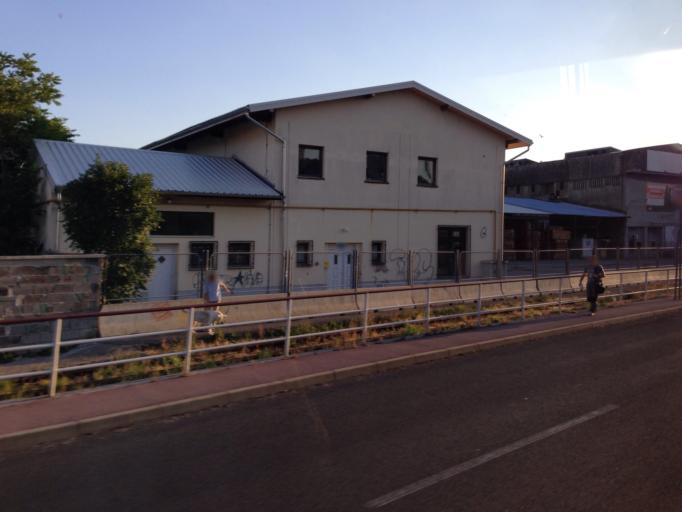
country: HR
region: Primorsko-Goranska
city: Drenova
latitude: 45.3239
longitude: 14.4471
